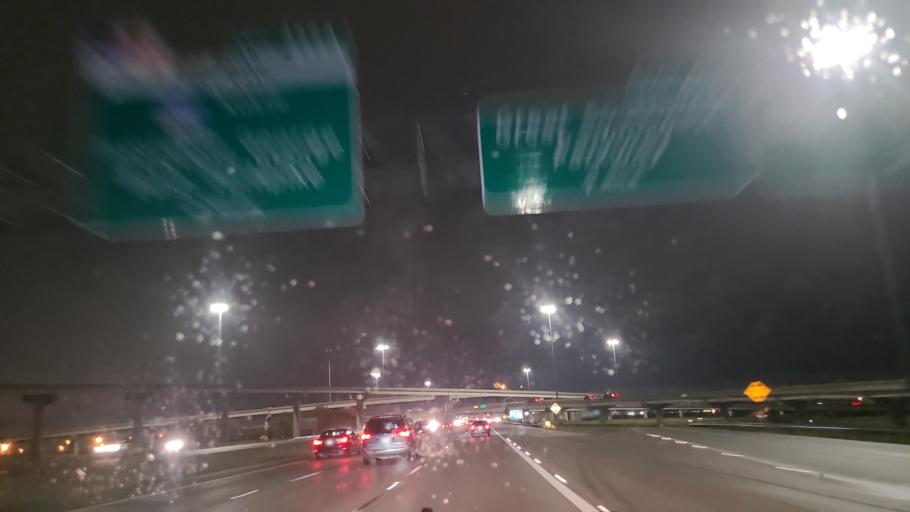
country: US
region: Texas
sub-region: Tarrant County
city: Arlington
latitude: 32.6772
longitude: -97.0664
